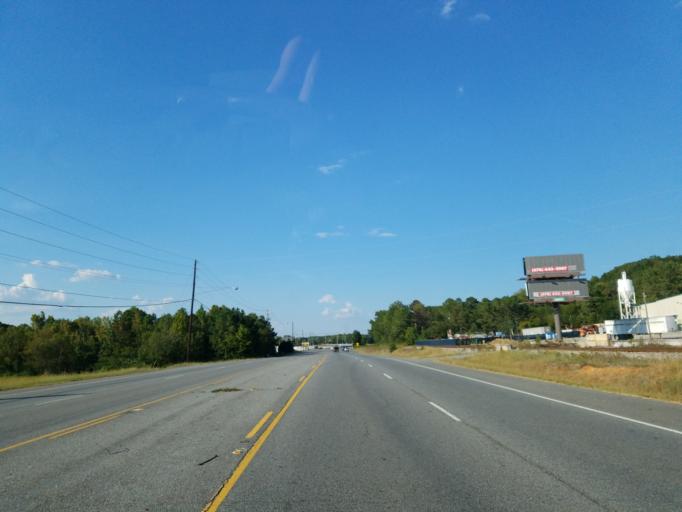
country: US
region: Georgia
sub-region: Murray County
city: Chatsworth
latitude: 34.7963
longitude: -84.7728
